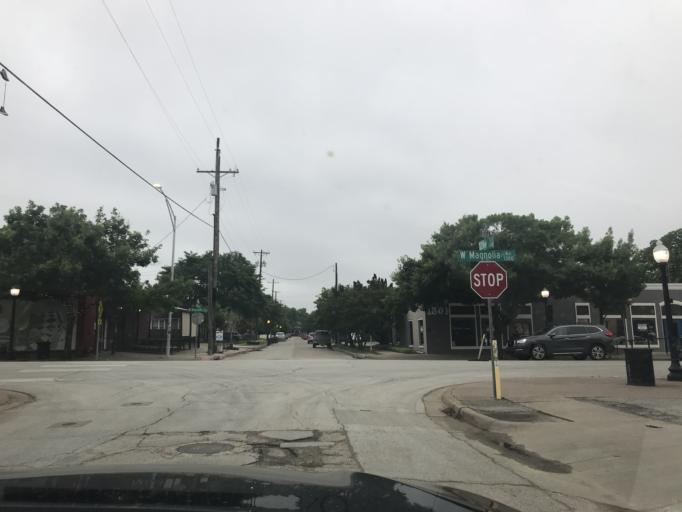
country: US
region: Texas
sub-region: Tarrant County
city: Fort Worth
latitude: 32.7308
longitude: -97.3394
